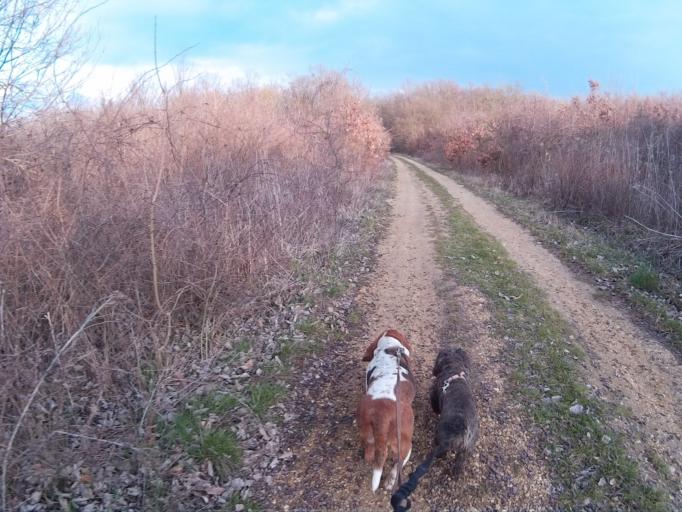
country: HU
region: Vas
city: Janoshaza
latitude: 47.1205
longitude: 17.0203
